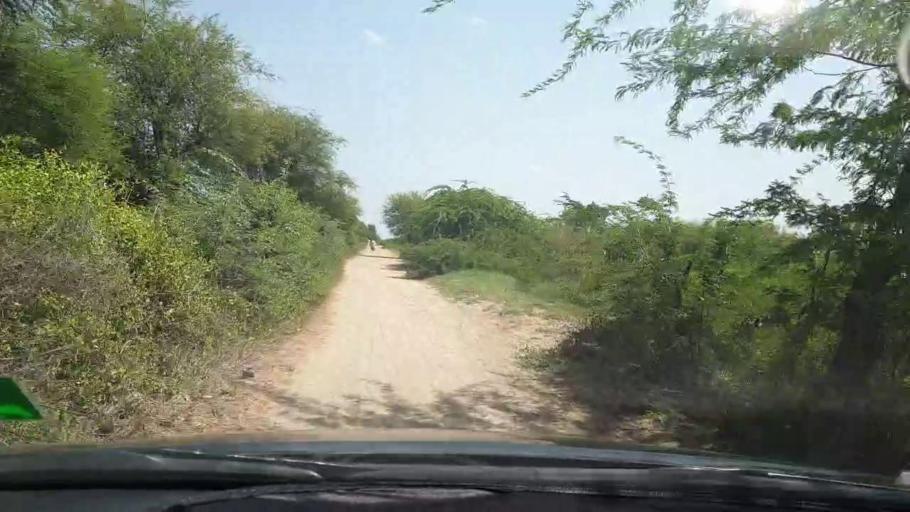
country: PK
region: Sindh
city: Tando Bago
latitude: 24.8967
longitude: 69.0817
